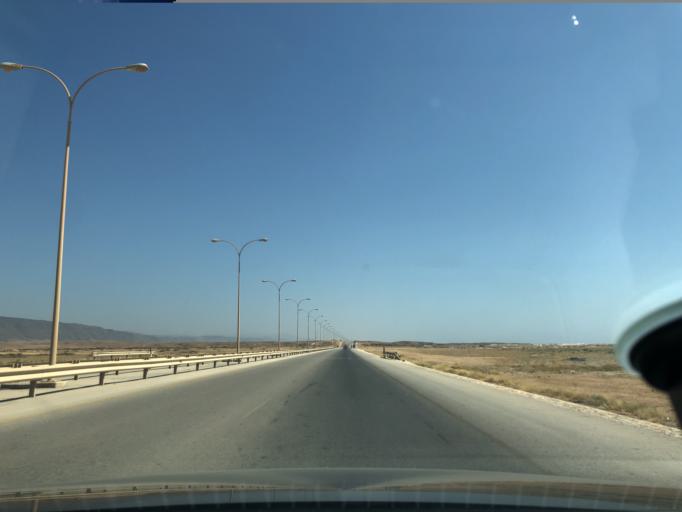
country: OM
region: Zufar
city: Salalah
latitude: 17.0521
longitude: 54.2979
